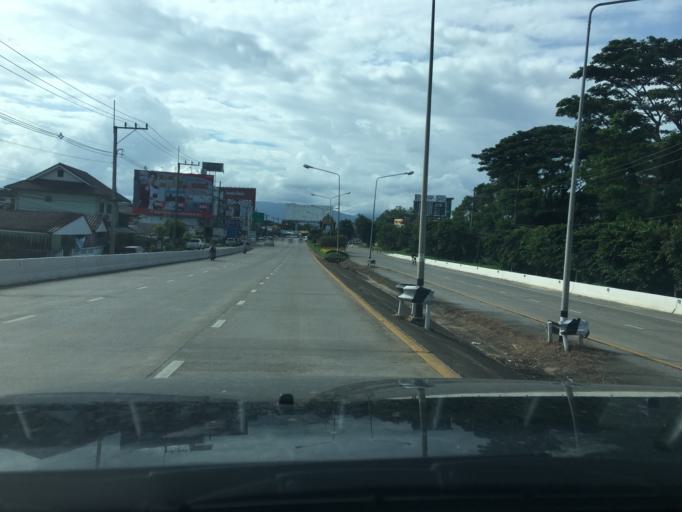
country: TH
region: Chiang Rai
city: Chiang Rai
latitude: 19.9225
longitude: 99.8454
